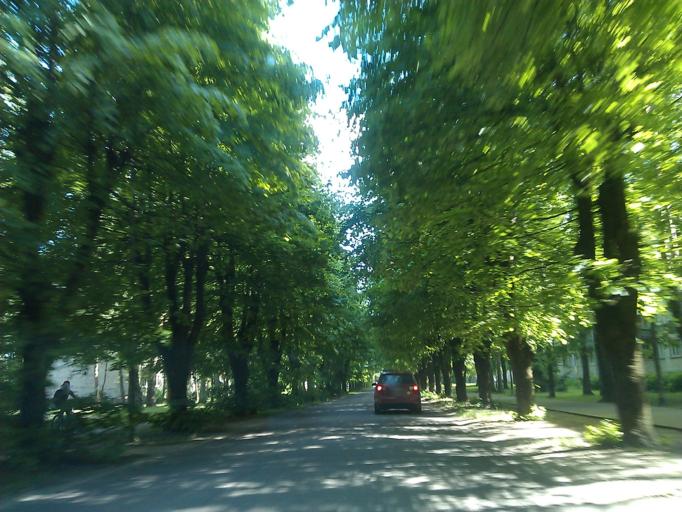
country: LV
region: Riga
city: Bergi
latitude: 56.9922
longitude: 24.2397
